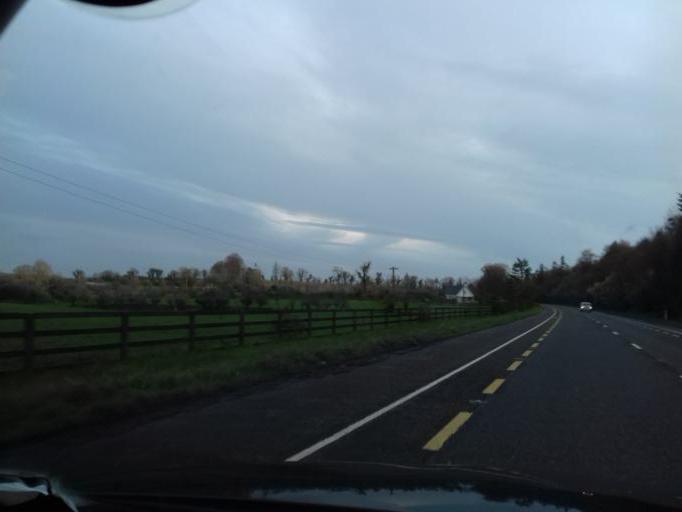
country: IE
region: Leinster
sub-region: Laois
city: Abbeyleix
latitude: 52.8750
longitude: -7.3616
